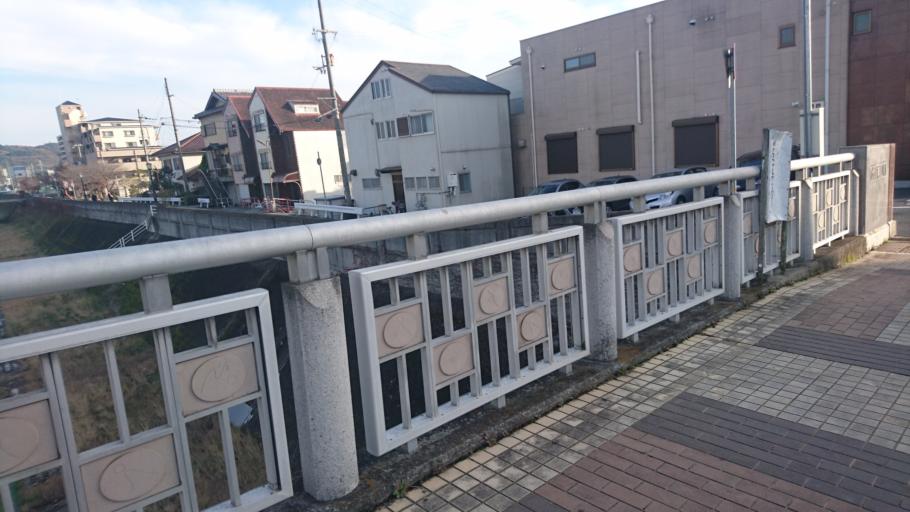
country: JP
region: Hyogo
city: Sandacho
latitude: 34.8851
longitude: 135.2285
